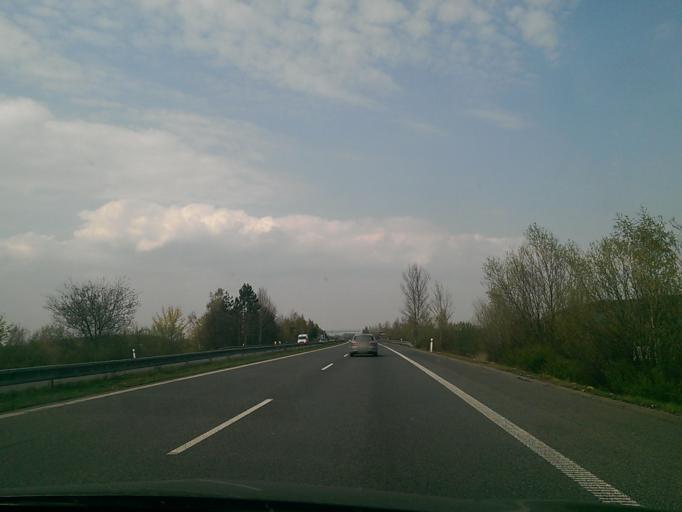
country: CZ
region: Central Bohemia
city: Mnichovo Hradiste
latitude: 50.4952
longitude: 14.9744
